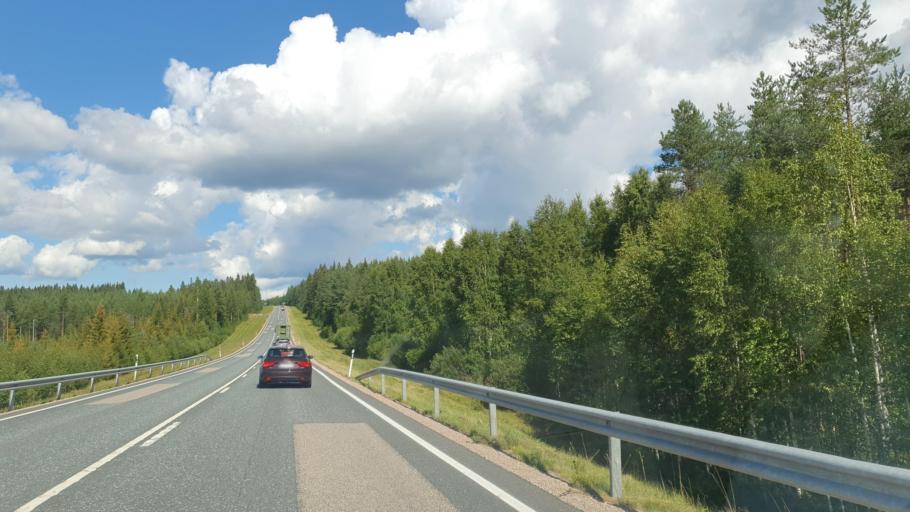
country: FI
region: Kainuu
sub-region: Kajaani
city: Kajaani
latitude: 64.0846
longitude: 27.4529
